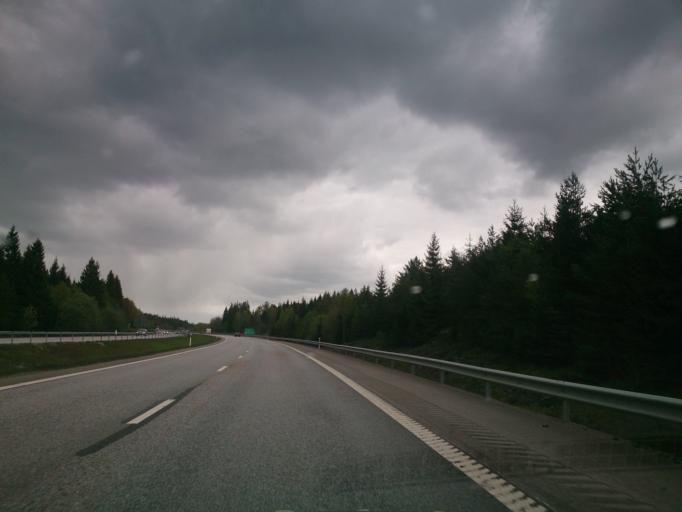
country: SE
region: Soedermanland
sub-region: Trosa Kommun
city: Vagnharad
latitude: 58.9796
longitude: 17.5306
